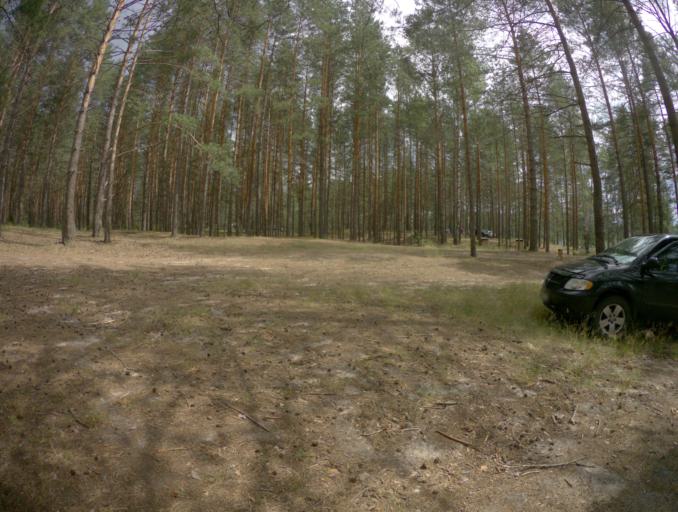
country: RU
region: Nizjnij Novgorod
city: Frolishchi
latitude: 56.3540
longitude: 42.7421
